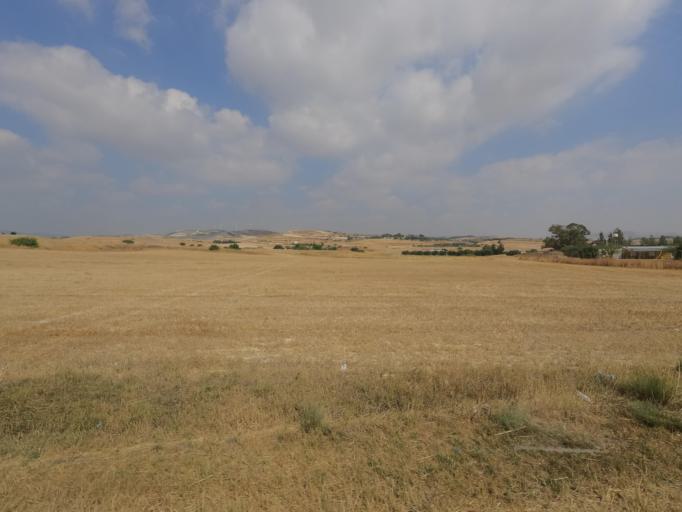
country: CY
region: Larnaka
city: Aradippou
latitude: 34.9419
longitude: 33.5561
